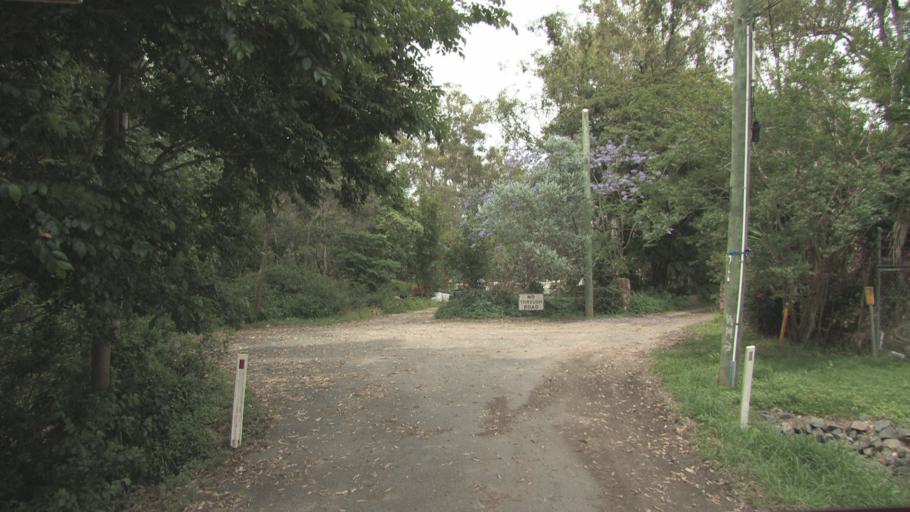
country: AU
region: Queensland
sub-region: Logan
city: Slacks Creek
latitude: -27.6510
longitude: 153.1522
